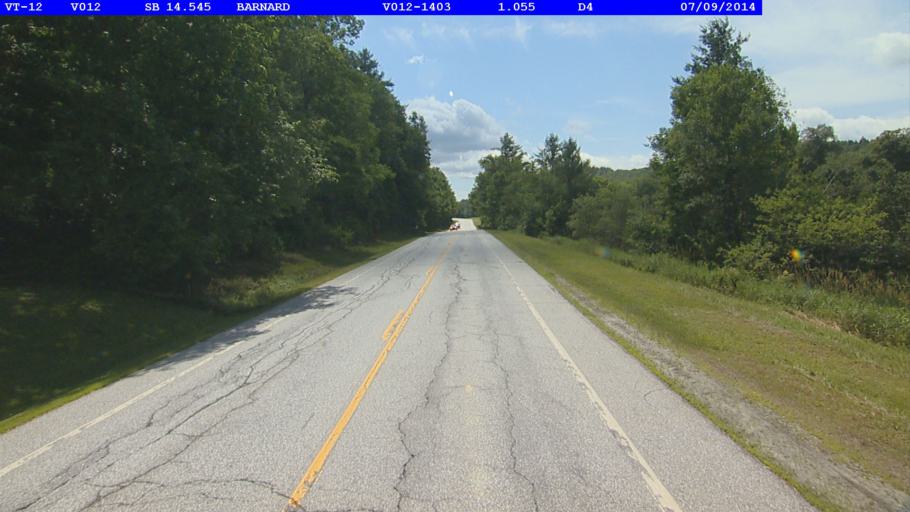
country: US
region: Vermont
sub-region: Windsor County
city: Woodstock
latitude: 43.6834
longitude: -72.5980
